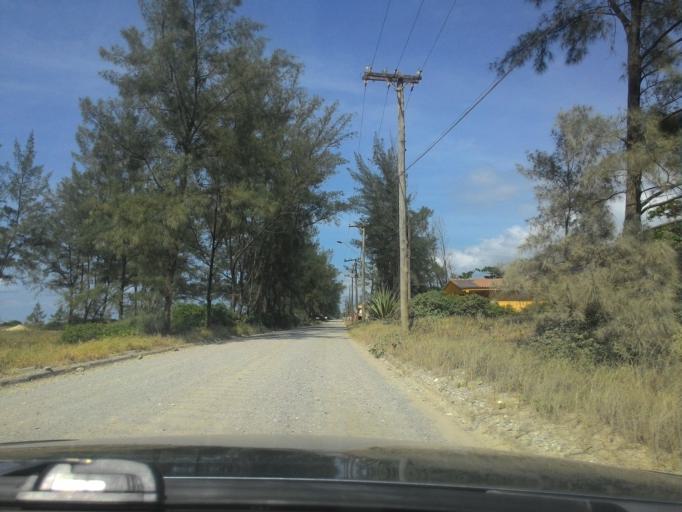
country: BR
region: Sao Paulo
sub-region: Iguape
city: Iguape
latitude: -24.8414
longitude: -47.6825
